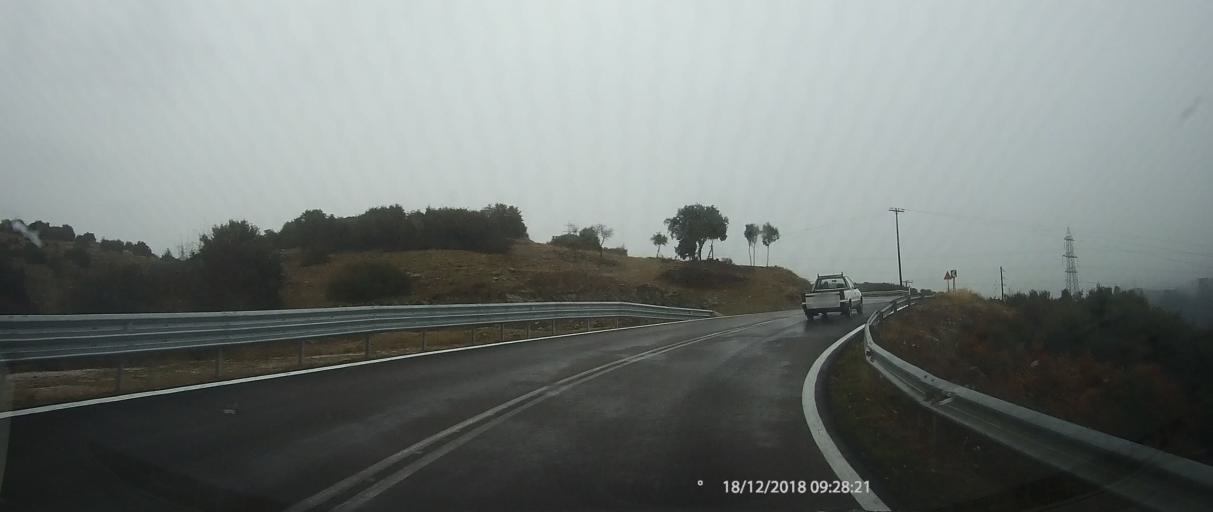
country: GR
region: Thessaly
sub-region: Nomos Larisis
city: Elassona
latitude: 39.9191
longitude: 22.1714
